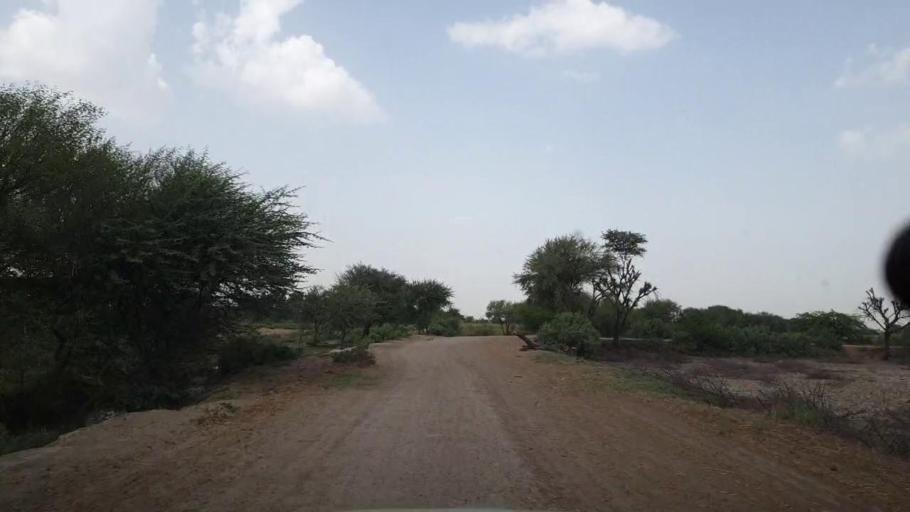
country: PK
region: Sindh
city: Tando Ghulam Ali
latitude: 25.0784
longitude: 68.8110
